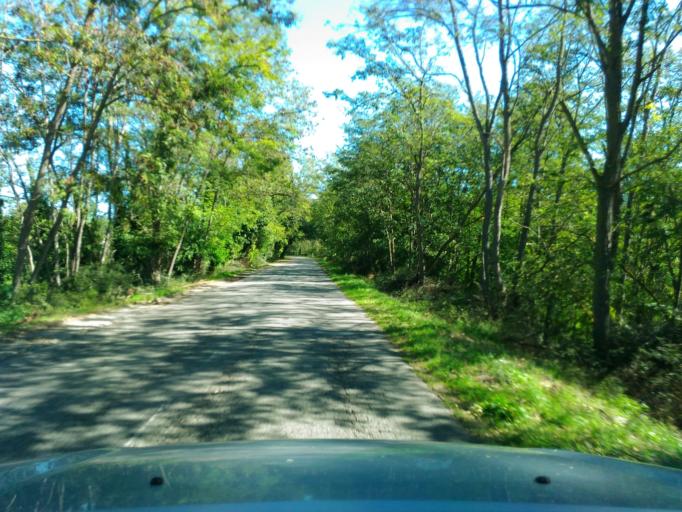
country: FR
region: Corsica
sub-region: Departement de la Haute-Corse
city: Aleria
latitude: 42.1159
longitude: 9.4865
